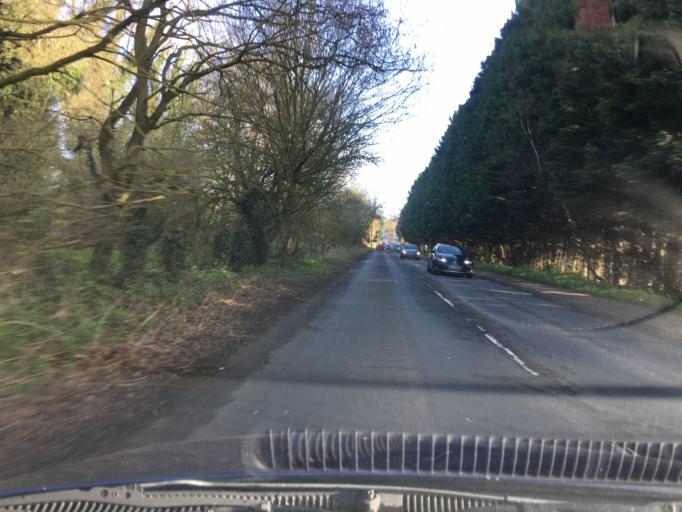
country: GB
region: England
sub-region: Bracknell Forest
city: Sandhurst
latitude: 51.3414
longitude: -0.8014
